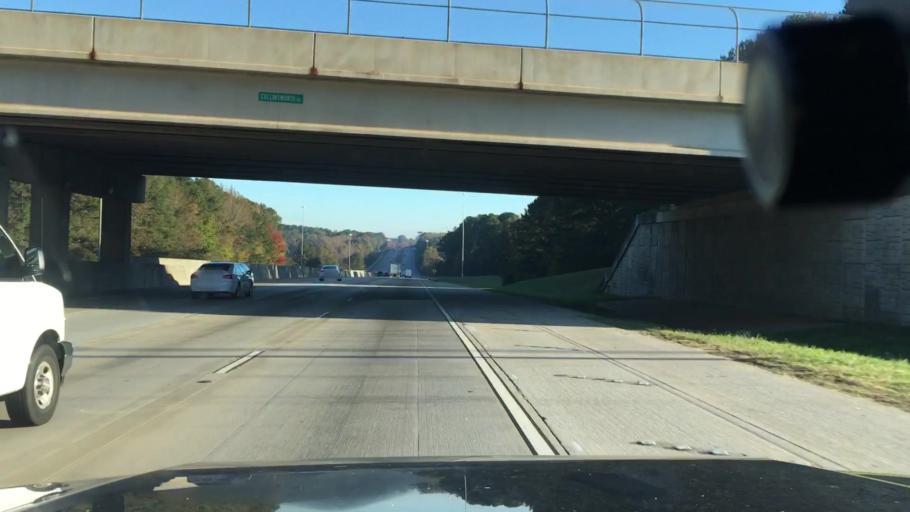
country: US
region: Georgia
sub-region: Fulton County
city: Palmetto
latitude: 33.4999
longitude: -84.6388
